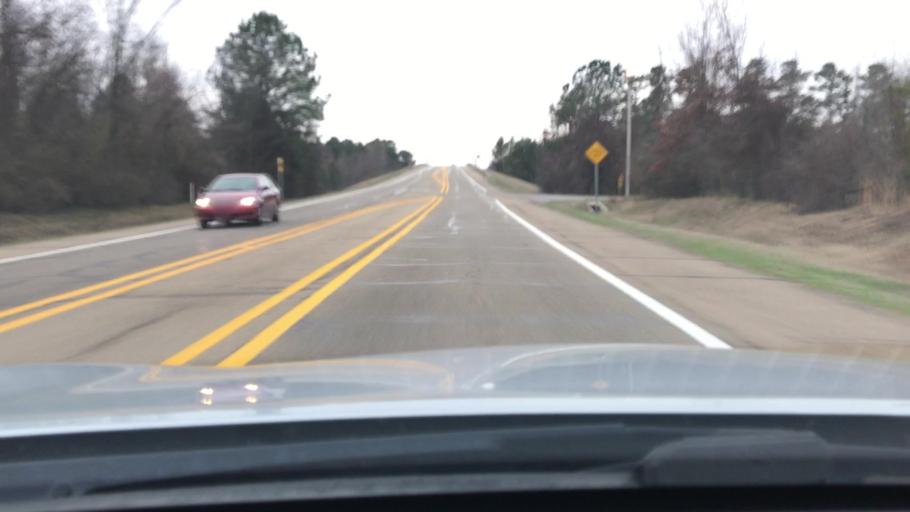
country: US
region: Arkansas
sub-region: Hempstead County
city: Hope
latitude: 33.6769
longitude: -93.5756
